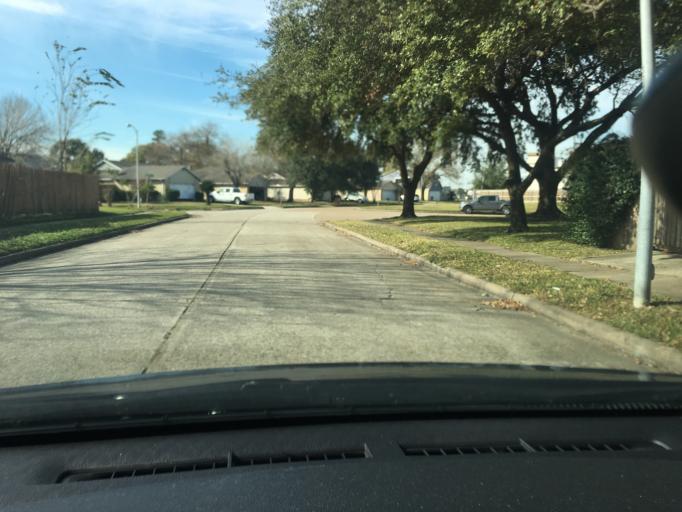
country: US
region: Texas
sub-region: Harris County
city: Cloverleaf
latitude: 29.8084
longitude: -95.1591
